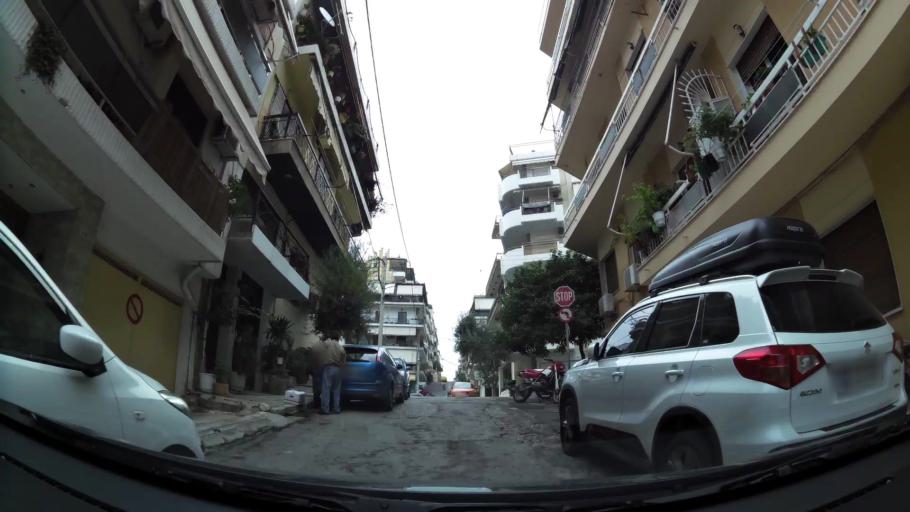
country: GR
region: Attica
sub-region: Nomos Attikis
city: Piraeus
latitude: 37.9338
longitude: 23.6307
